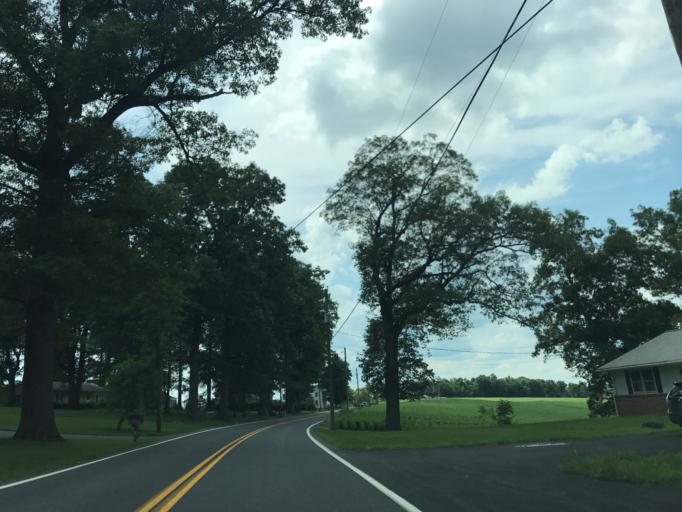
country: US
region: Pennsylvania
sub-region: Lancaster County
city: Penryn
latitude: 40.2044
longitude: -76.3976
